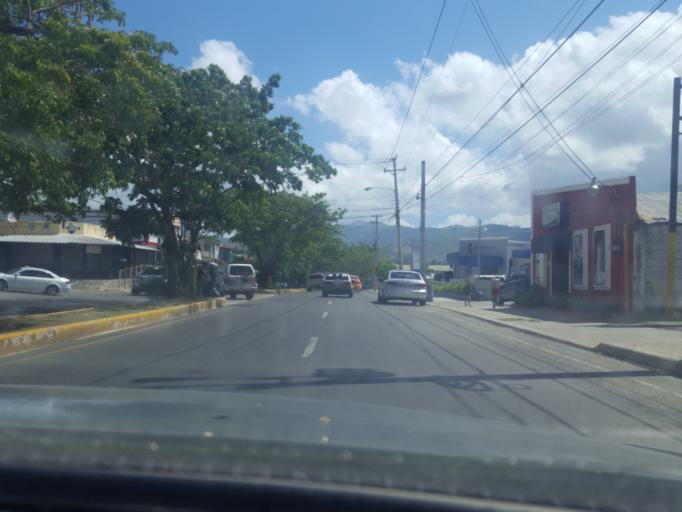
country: DO
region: Santiago
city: Santiago de los Caballeros
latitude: 19.4857
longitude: -70.7042
